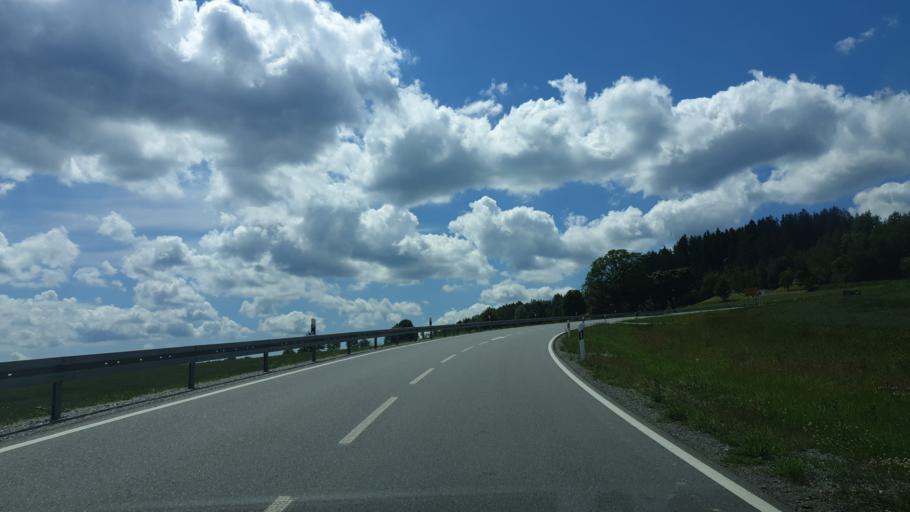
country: DE
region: Saxony
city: Schwarzenberg
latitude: 50.5260
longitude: 12.7679
